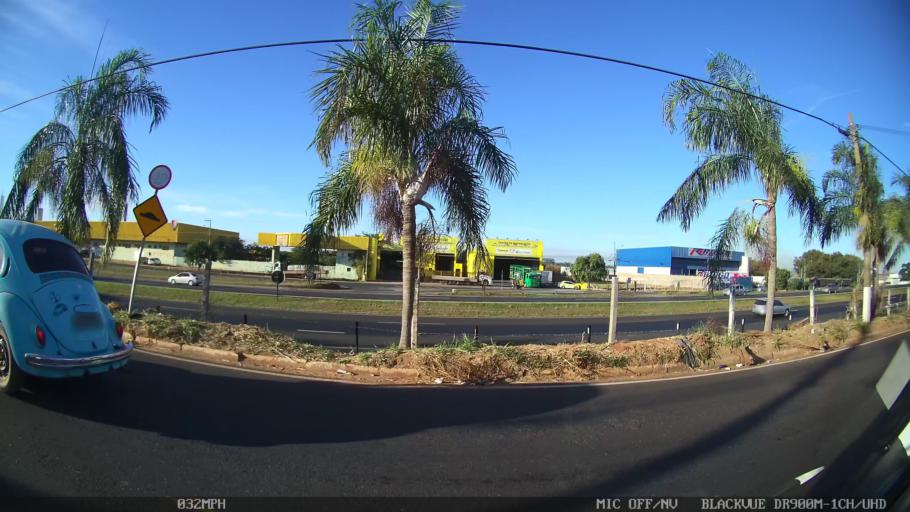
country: BR
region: Sao Paulo
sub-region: Sao Jose Do Rio Preto
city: Sao Jose do Rio Preto
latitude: -20.8522
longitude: -49.3428
